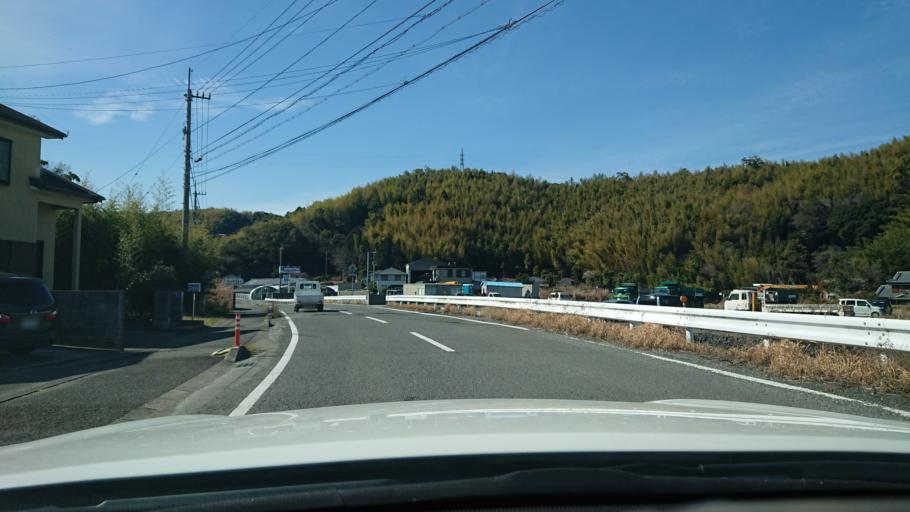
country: JP
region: Tokushima
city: Komatsushimacho
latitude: 33.9705
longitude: 134.5987
